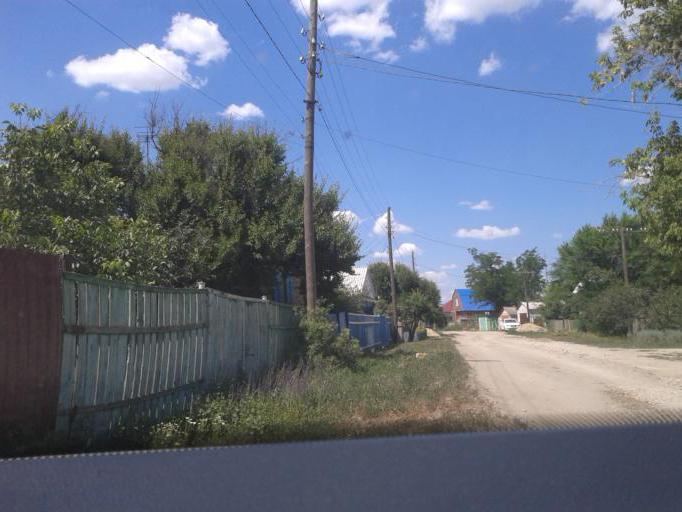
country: RU
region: Volgograd
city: Frolovo
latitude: 49.7626
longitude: 43.6614
